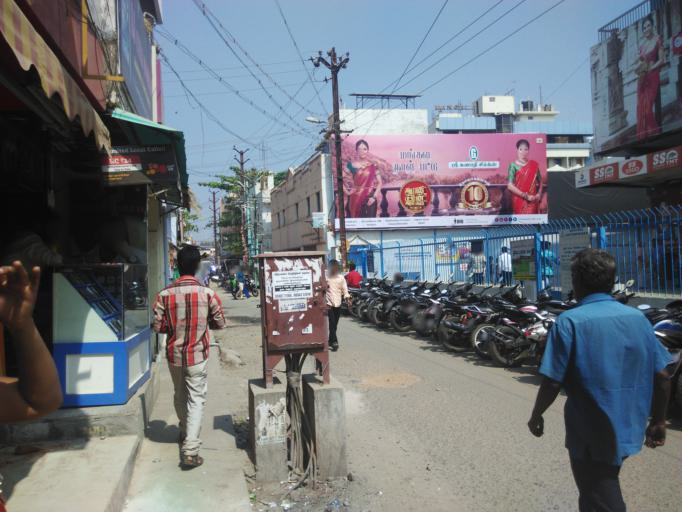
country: IN
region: Tamil Nadu
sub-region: Coimbatore
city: Coimbatore
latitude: 11.0147
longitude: 76.9646
